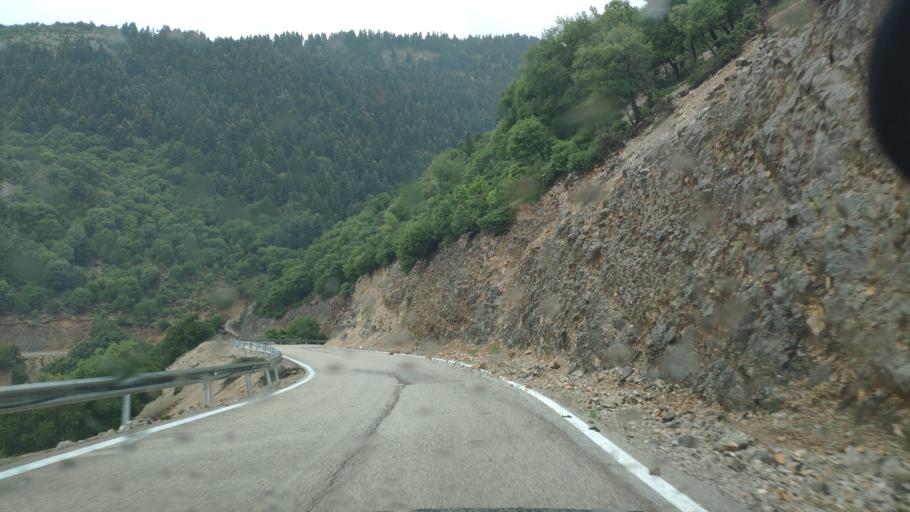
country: GR
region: West Greece
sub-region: Nomos Aitolias kai Akarnanias
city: Krikellos
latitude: 39.0344
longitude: 21.3687
